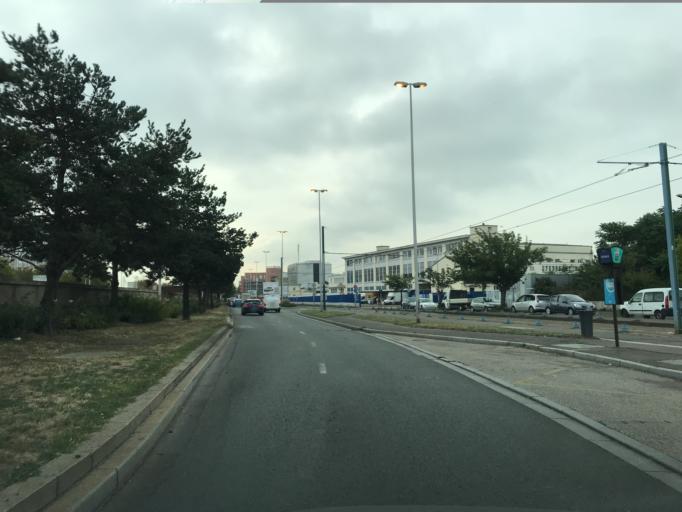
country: FR
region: Ile-de-France
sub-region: Departement de Seine-Saint-Denis
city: Drancy
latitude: 48.9141
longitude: 2.4316
